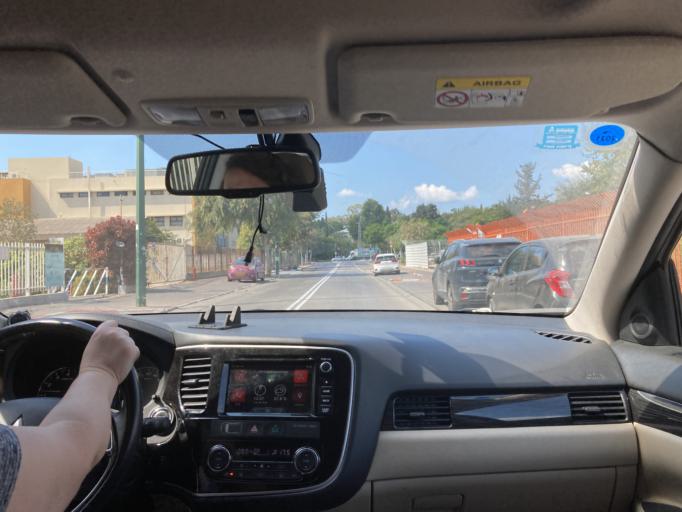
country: IL
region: Tel Aviv
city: Bene Beraq
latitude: 32.1116
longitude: 34.8406
